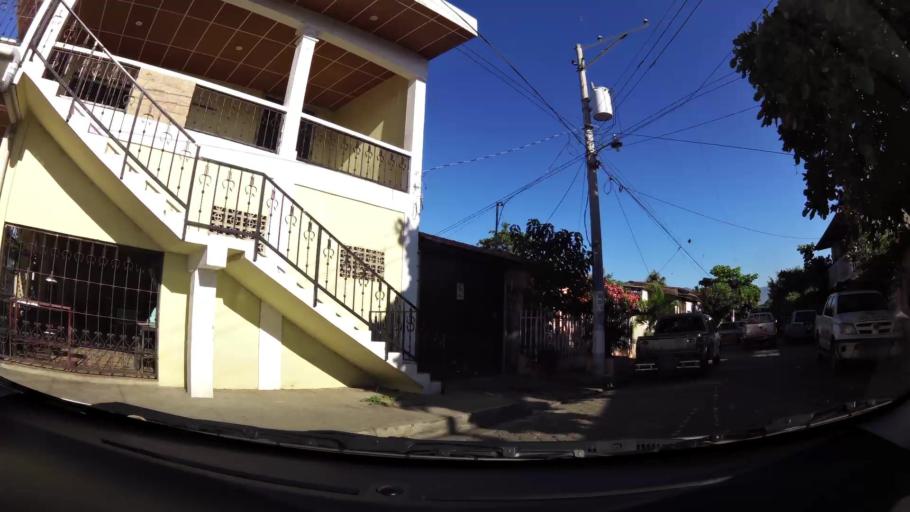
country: SV
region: Sonsonate
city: Sonsonate
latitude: 13.7044
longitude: -89.7150
